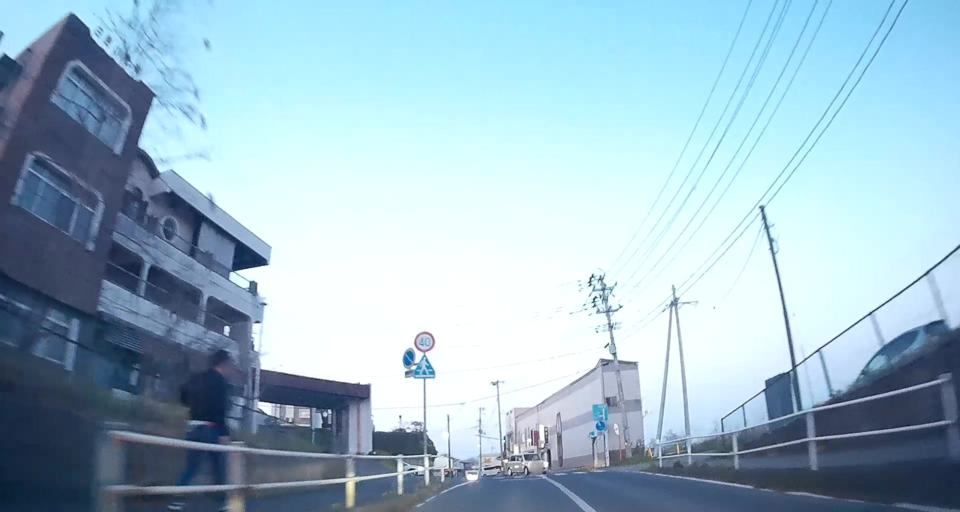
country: JP
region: Aomori
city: Hachinohe
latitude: 40.1884
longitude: 141.7720
